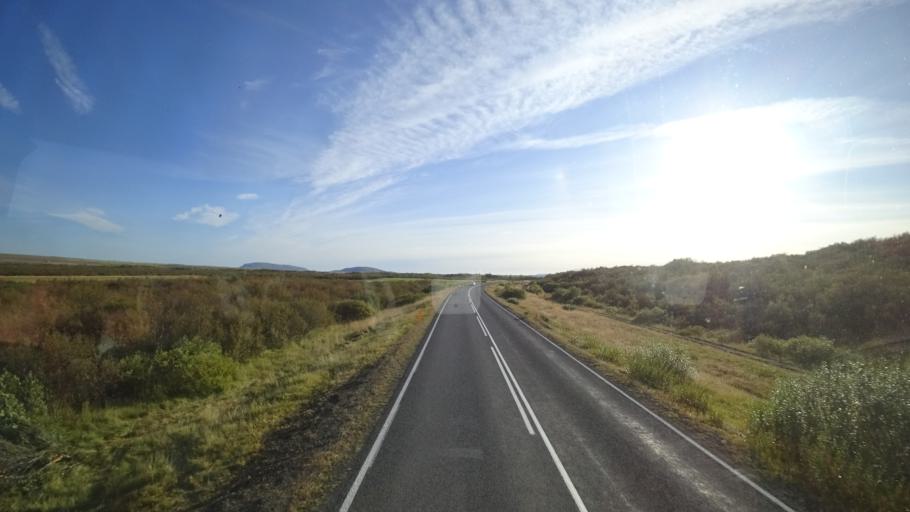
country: IS
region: South
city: Selfoss
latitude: 64.2279
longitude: -20.5697
